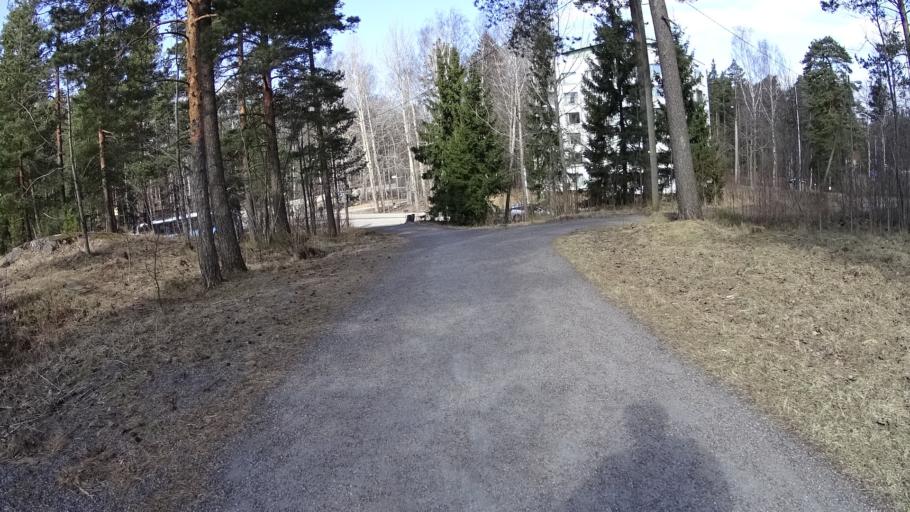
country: FI
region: Uusimaa
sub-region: Helsinki
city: Kilo
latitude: 60.2272
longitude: 24.7581
